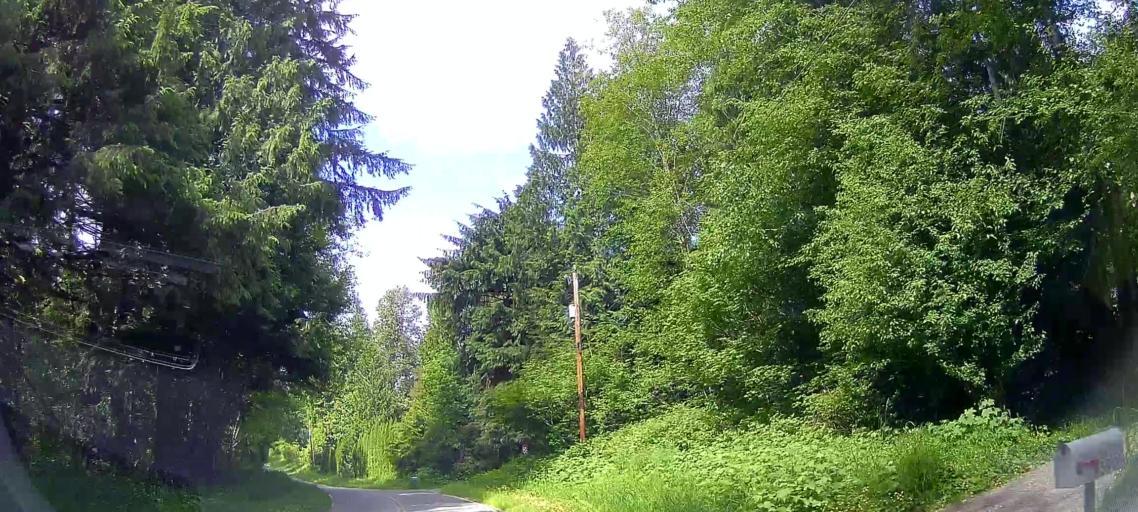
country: US
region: Washington
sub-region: Whatcom County
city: Sudden Valley
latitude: 48.6644
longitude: -122.1958
